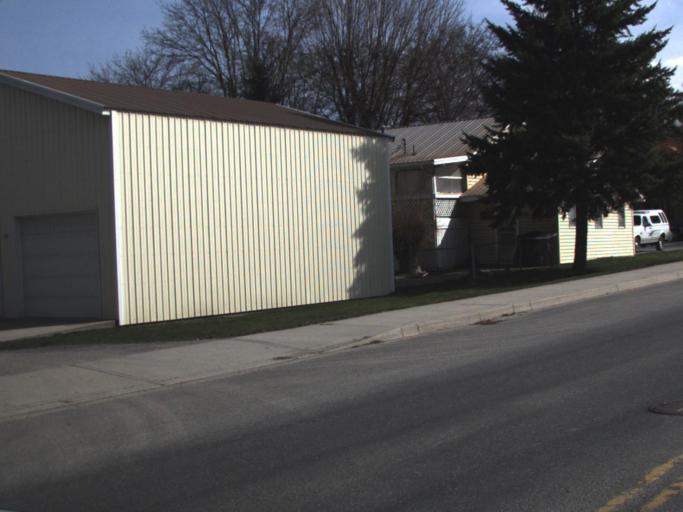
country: US
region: Washington
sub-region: Stevens County
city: Colville
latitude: 48.5466
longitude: -117.9037
